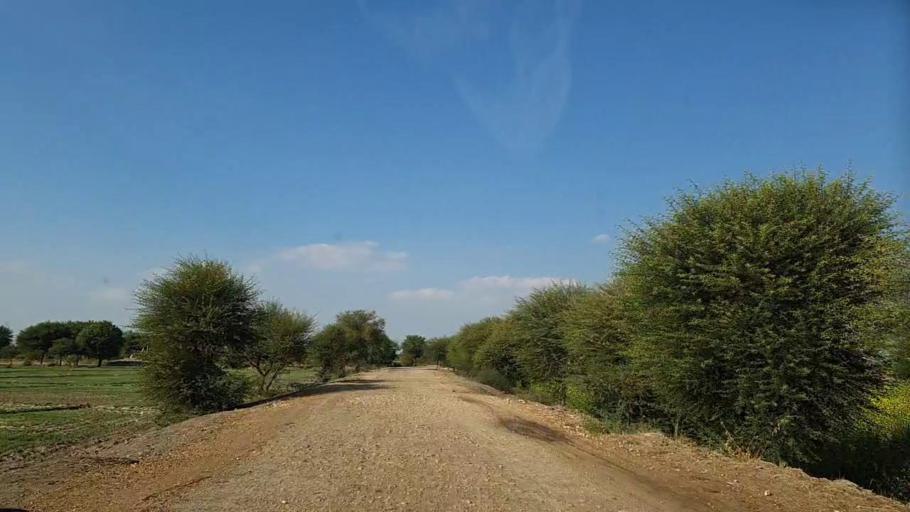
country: PK
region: Sindh
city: Pithoro
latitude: 25.6275
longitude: 69.3523
